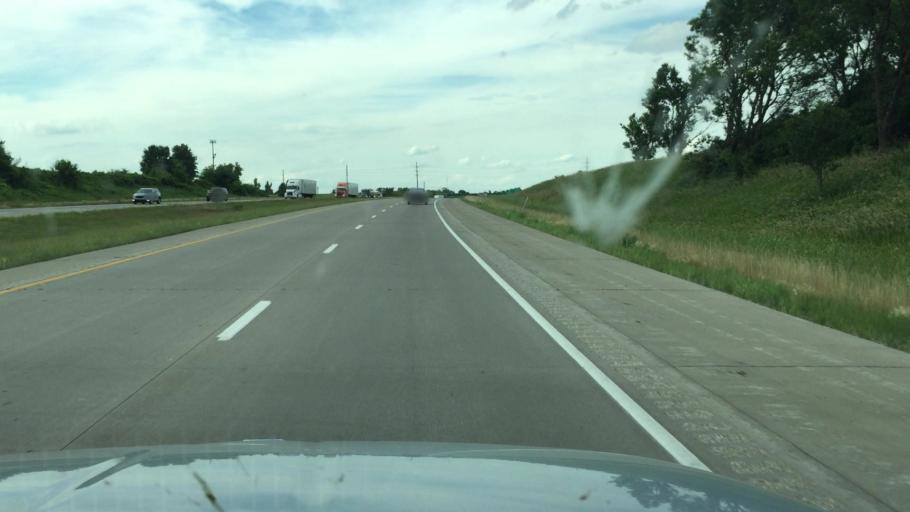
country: US
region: Iowa
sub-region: Scott County
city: Walcott
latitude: 41.5650
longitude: -90.6788
